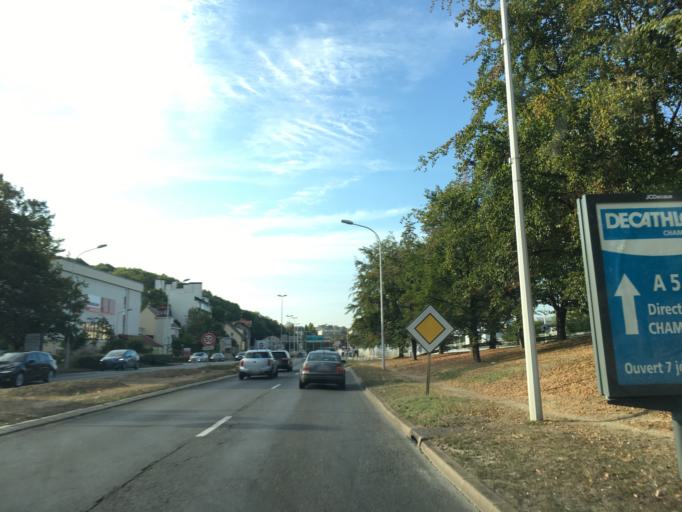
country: FR
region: Ile-de-France
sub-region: Departement des Yvelines
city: Le Port-Marly
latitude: 48.8808
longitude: 2.1091
